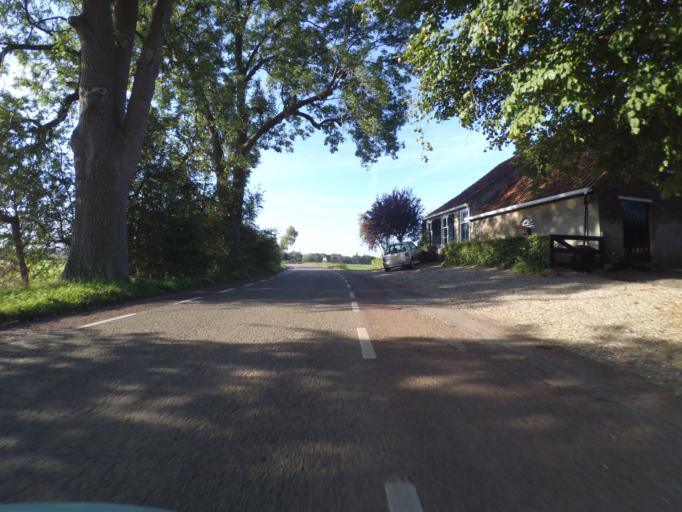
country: NL
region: Utrecht
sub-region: Gemeente Utrechtse Heuvelrug
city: Amerongen
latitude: 51.9886
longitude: 5.4579
